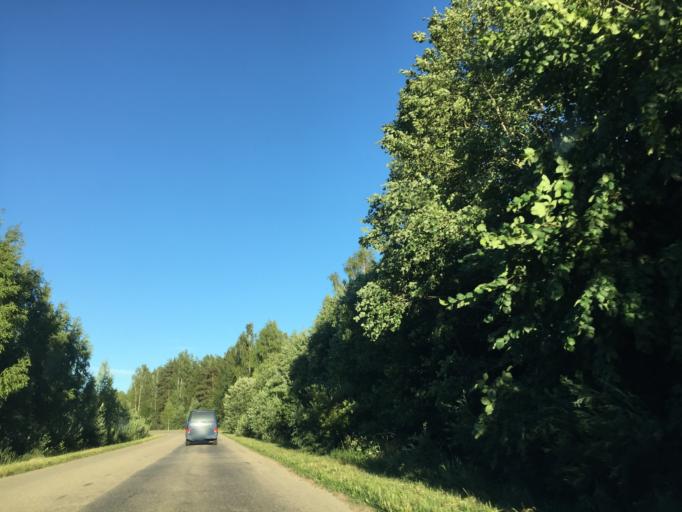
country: LV
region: Jekabpils Rajons
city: Jekabpils
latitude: 56.6088
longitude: 25.8372
